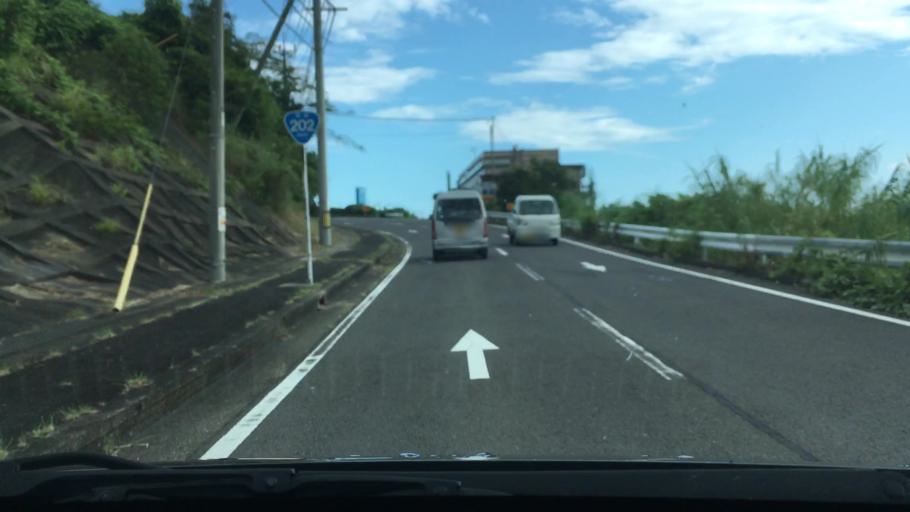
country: JP
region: Nagasaki
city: Togitsu
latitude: 32.8698
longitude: 129.6786
